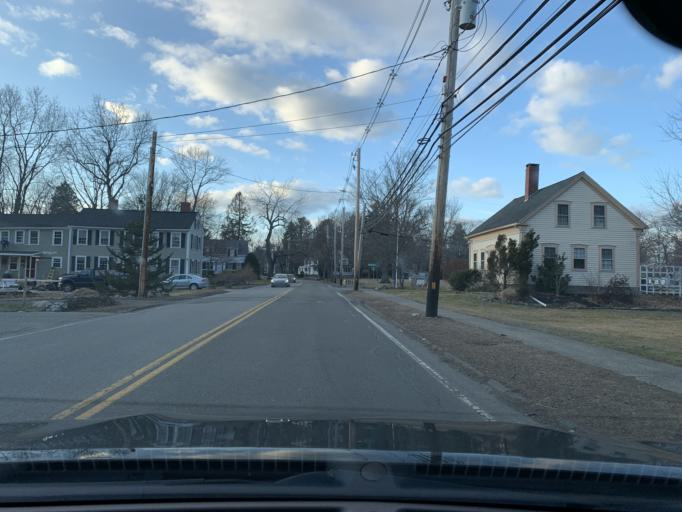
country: US
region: Massachusetts
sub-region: Essex County
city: Danvers
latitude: 42.5665
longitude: -70.9641
